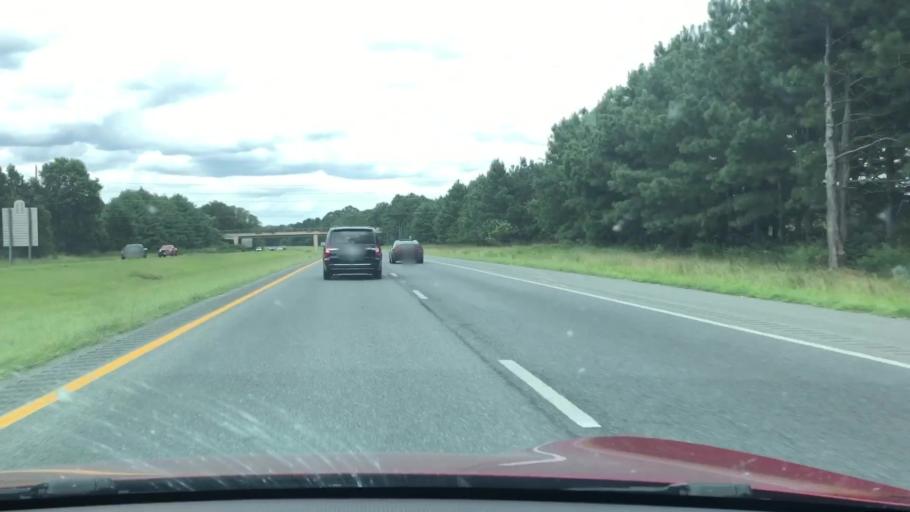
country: US
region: Maryland
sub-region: Wicomico County
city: Salisbury
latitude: 38.3399
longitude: -75.5528
